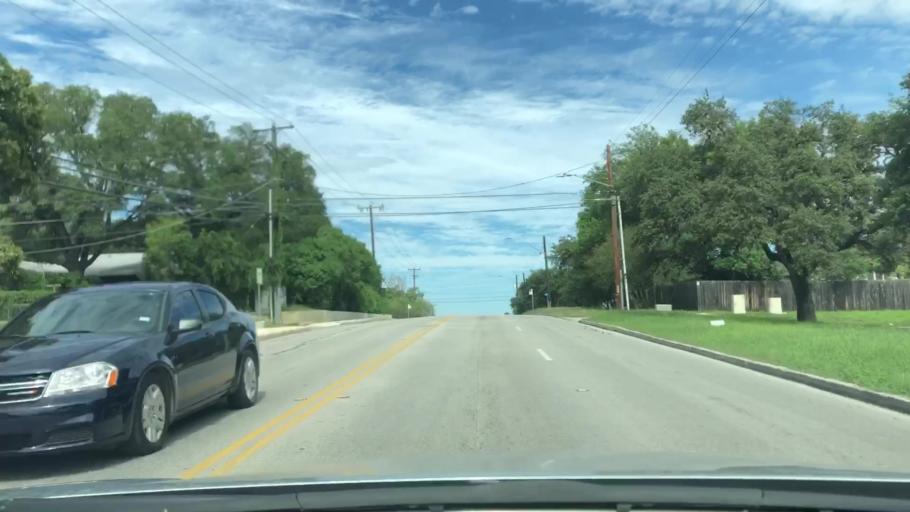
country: US
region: Texas
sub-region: Bexar County
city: Olmos Park
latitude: 29.4993
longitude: -98.4916
